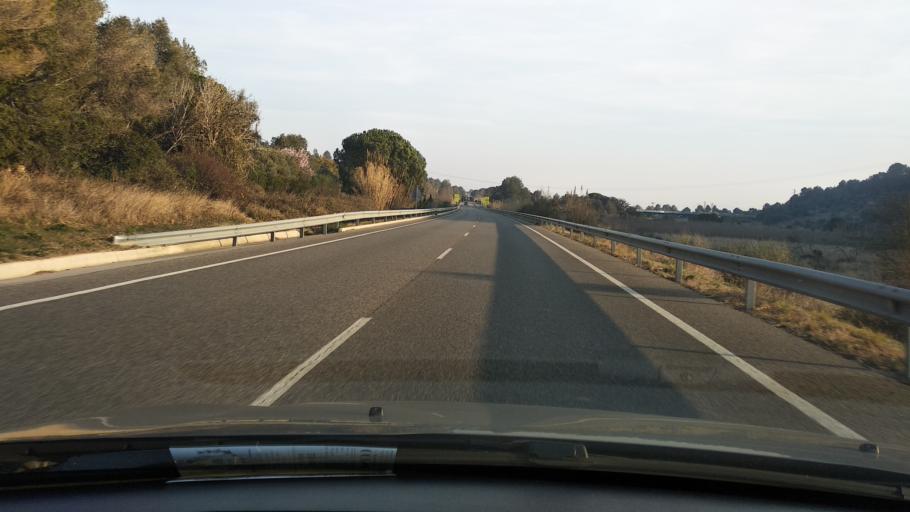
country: ES
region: Catalonia
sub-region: Provincia de Tarragona
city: les Borges del Camp
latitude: 41.1854
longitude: 1.0053
